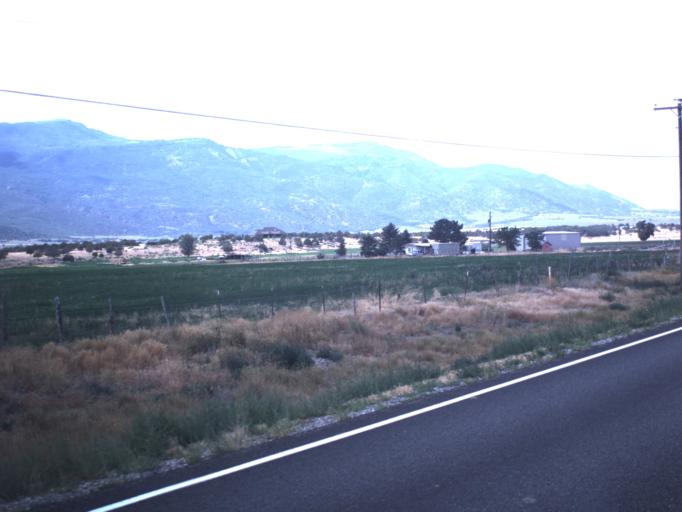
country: US
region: Utah
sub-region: Sanpete County
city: Fountain Green
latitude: 39.5928
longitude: -111.6180
